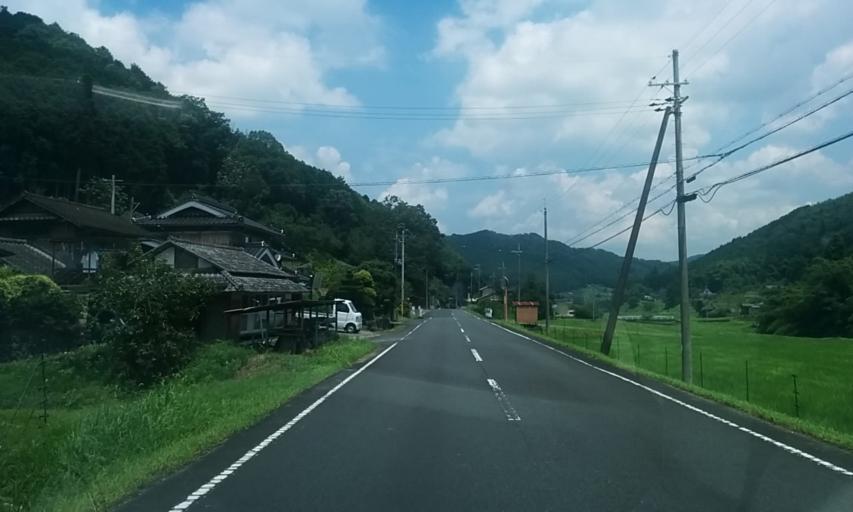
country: JP
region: Kyoto
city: Ayabe
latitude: 35.2030
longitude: 135.2236
